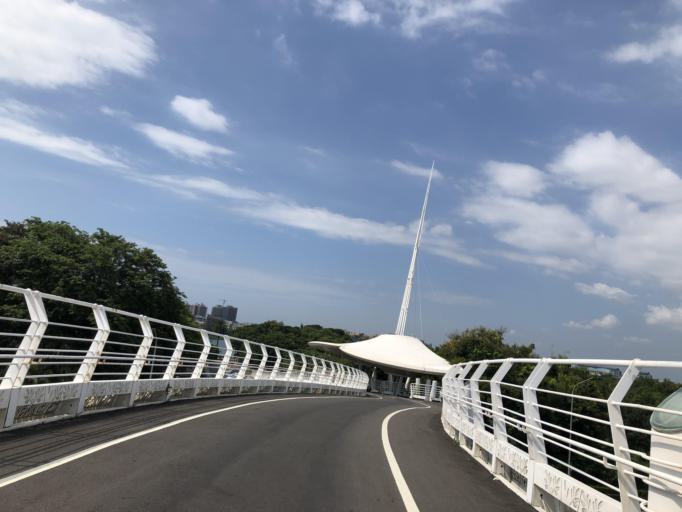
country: TW
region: Kaohsiung
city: Kaohsiung
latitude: 22.6796
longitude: 120.2988
